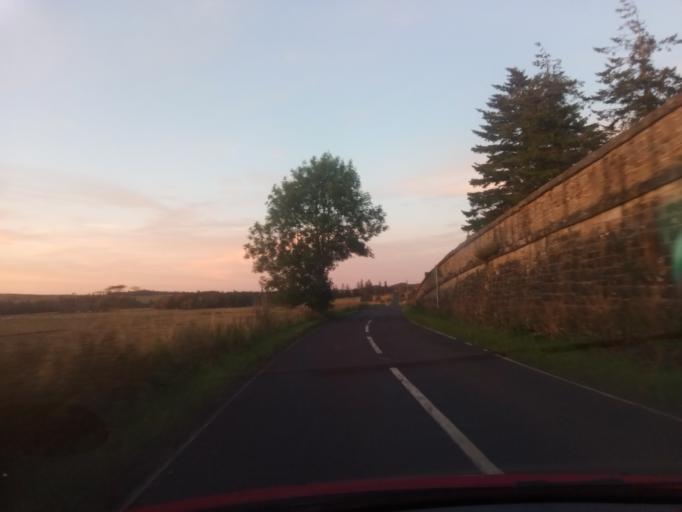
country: GB
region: England
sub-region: Northumberland
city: Bardon Mill
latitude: 54.9311
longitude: -2.3045
